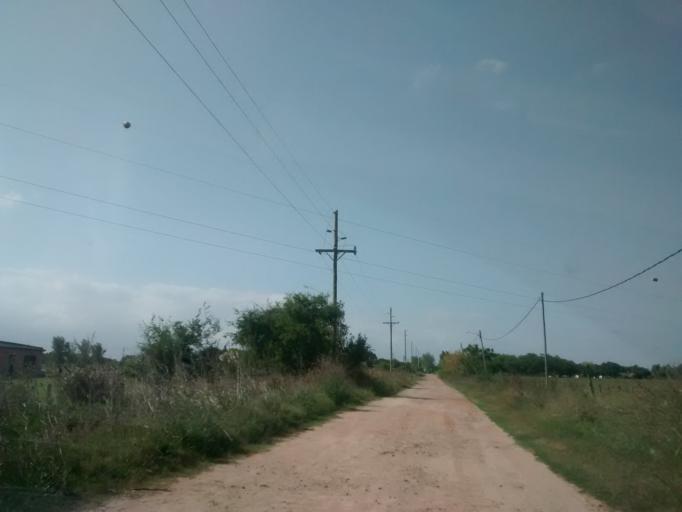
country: AR
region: Buenos Aires
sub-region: Partido de La Plata
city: La Plata
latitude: -35.0059
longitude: -57.9026
